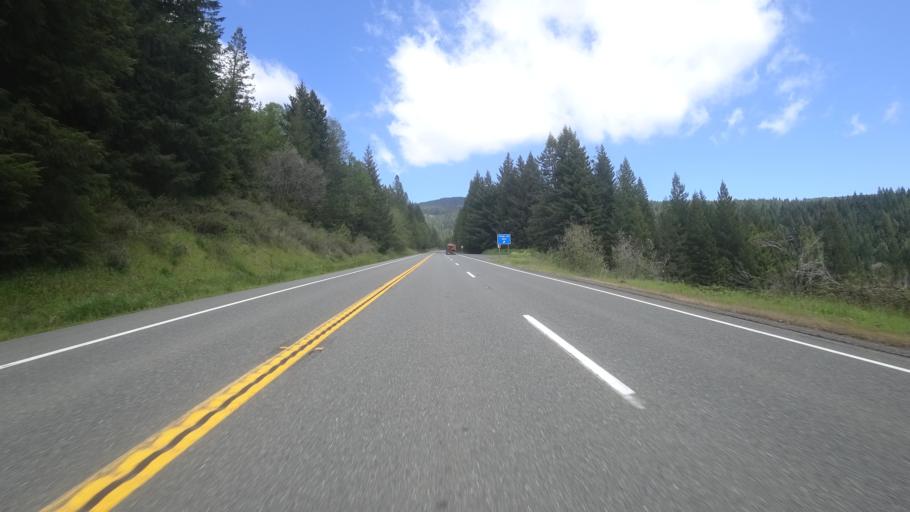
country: US
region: California
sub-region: Humboldt County
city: Blue Lake
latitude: 40.9431
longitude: -123.9001
